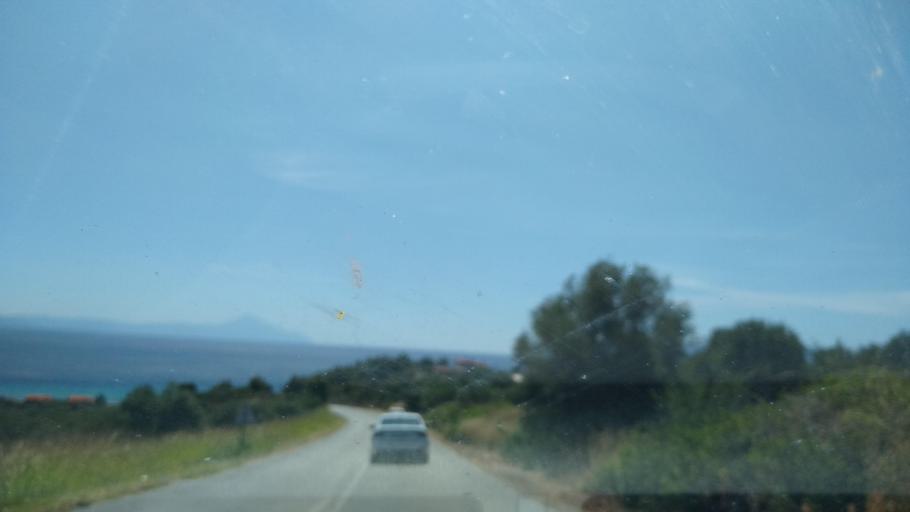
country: GR
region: Central Macedonia
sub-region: Nomos Chalkidikis
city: Agios Nikolaos
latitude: 40.3042
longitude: 23.6878
